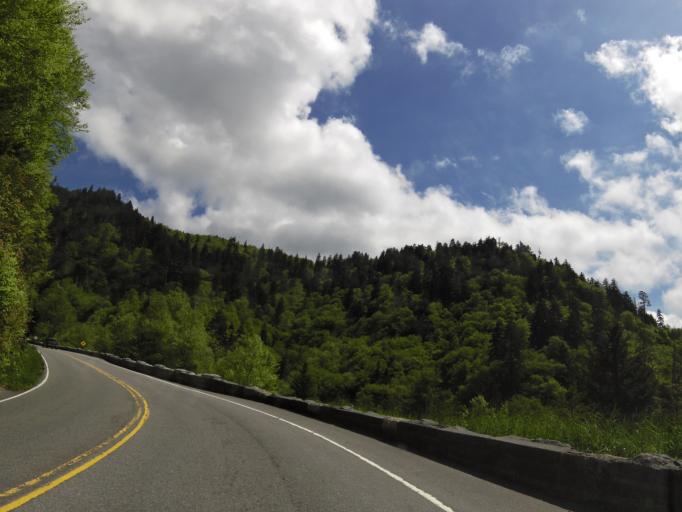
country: US
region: Tennessee
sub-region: Sevier County
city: Gatlinburg
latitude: 35.6194
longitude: -83.4208
